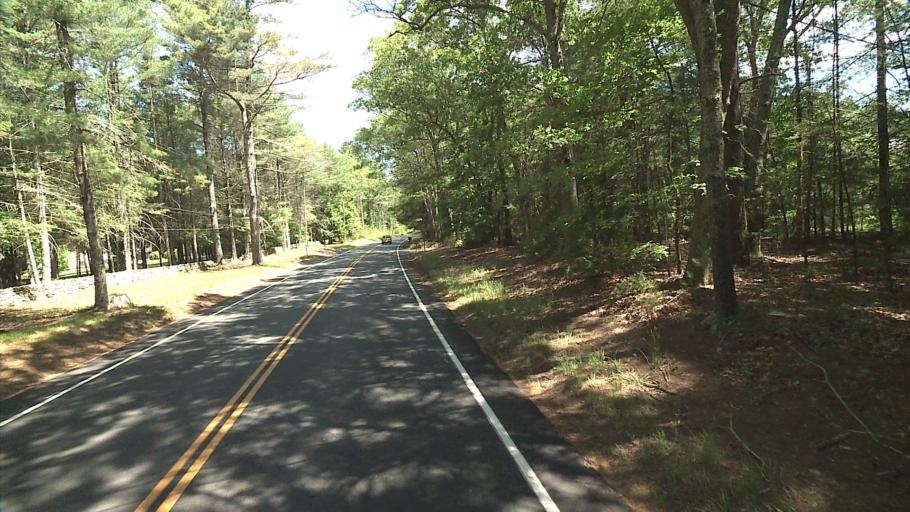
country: US
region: Connecticut
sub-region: Windham County
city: Plainfield
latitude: 41.5972
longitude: -71.8552
